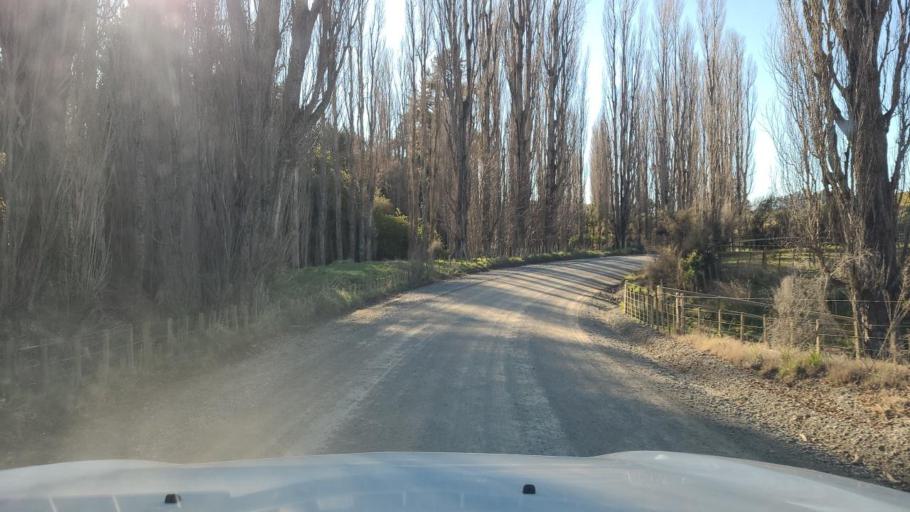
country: NZ
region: Hawke's Bay
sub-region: Napier City
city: Taradale
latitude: -39.3755
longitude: 176.5673
